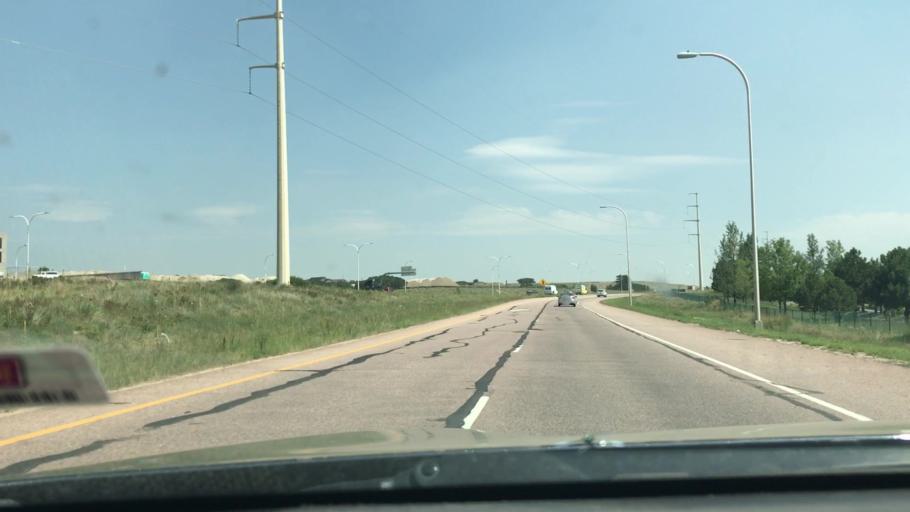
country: US
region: Colorado
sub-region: El Paso County
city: Black Forest
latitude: 38.9823
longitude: -104.7629
